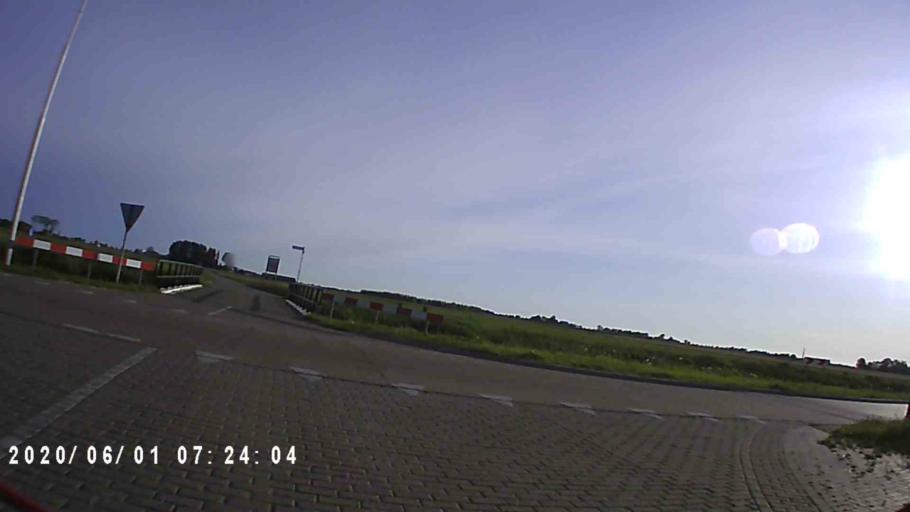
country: NL
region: Friesland
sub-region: Gemeente Dantumadiel
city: Walterswald
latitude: 53.3167
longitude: 6.0313
